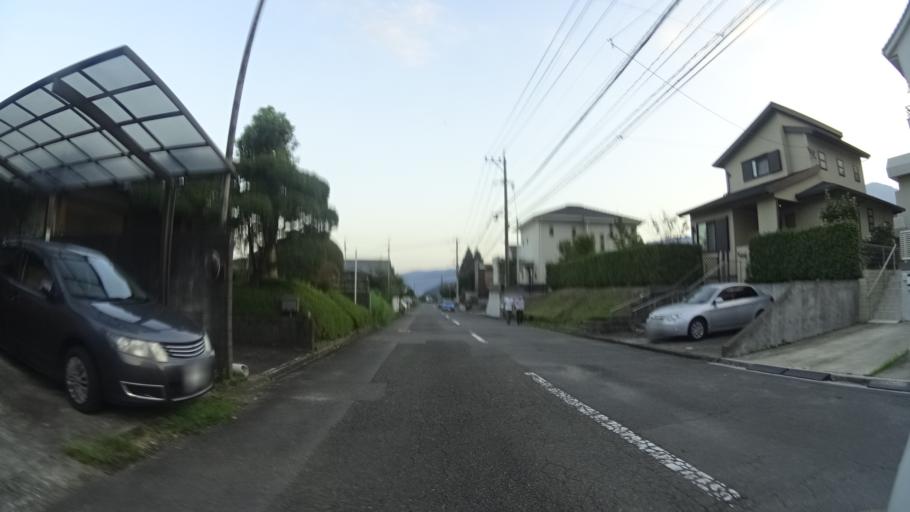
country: JP
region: Oita
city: Beppu
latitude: 33.3178
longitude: 131.4845
